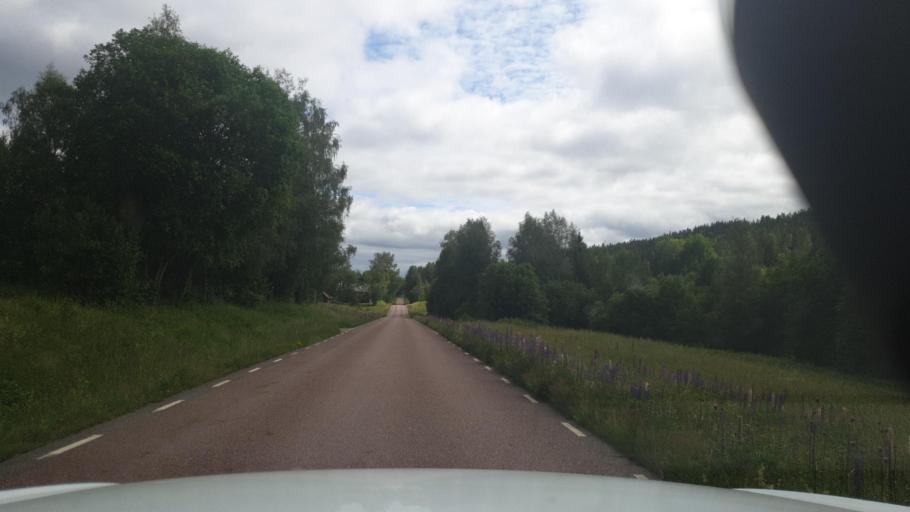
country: NO
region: Ostfold
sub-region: Romskog
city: Romskog
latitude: 59.7348
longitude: 12.0610
